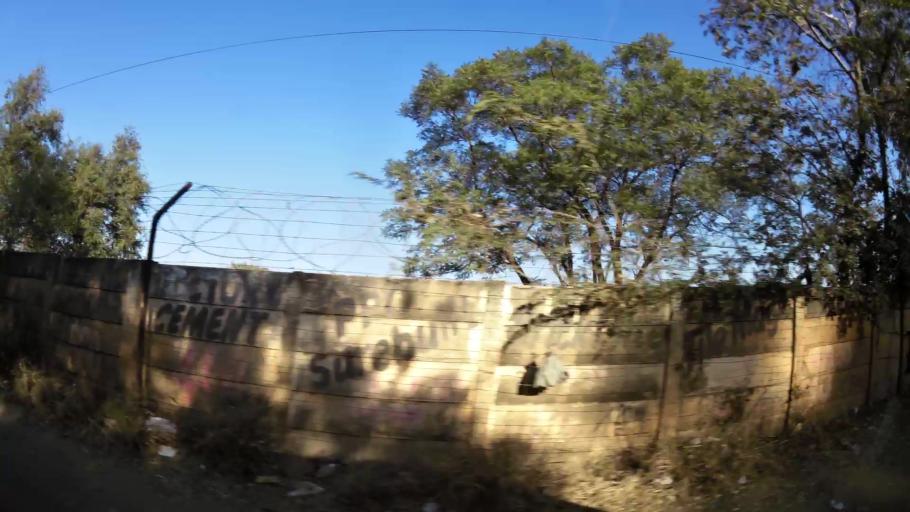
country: ZA
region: Gauteng
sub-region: City of Tshwane Metropolitan Municipality
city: Pretoria
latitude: -25.6291
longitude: 28.2053
